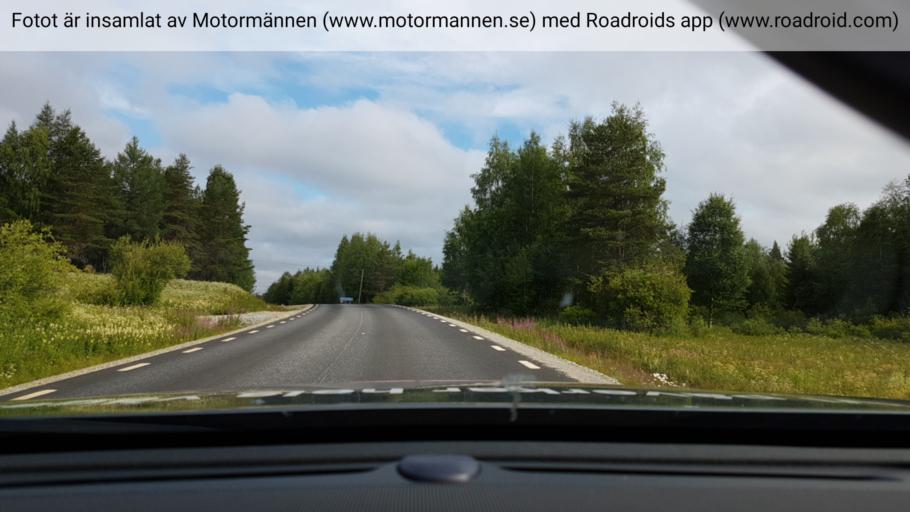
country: SE
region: Vaesterbotten
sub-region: Vindelns Kommun
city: Vindeln
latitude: 64.4500
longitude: 19.3397
